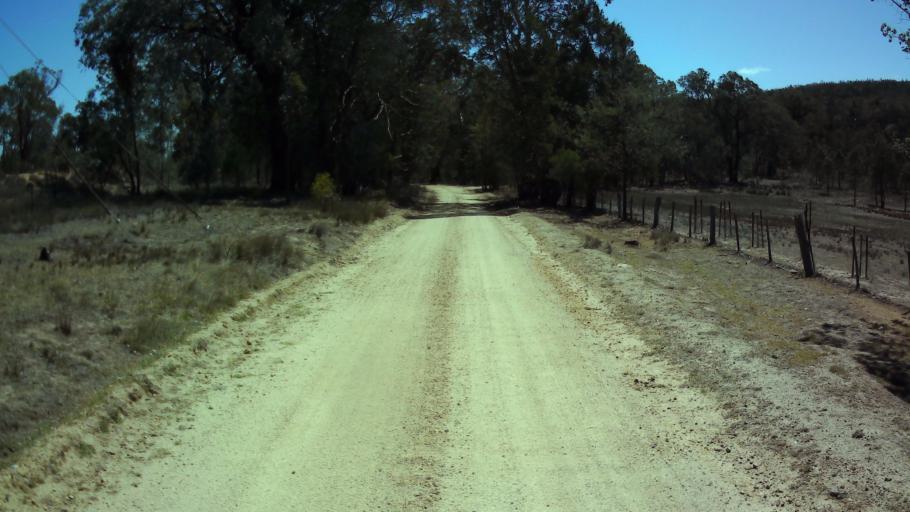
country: AU
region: New South Wales
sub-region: Cowra
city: Cowra
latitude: -33.8381
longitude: 148.4521
